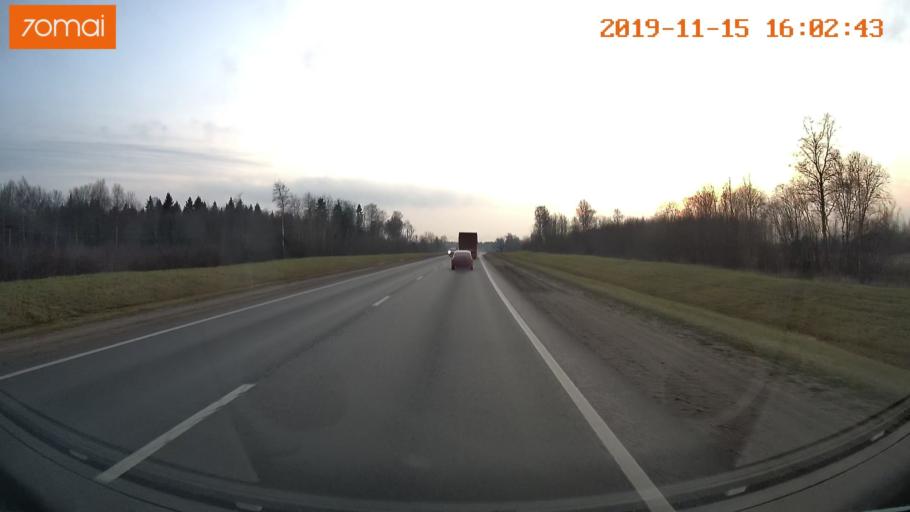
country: RU
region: Jaroslavl
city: Yaroslavl
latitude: 57.7684
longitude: 39.9221
